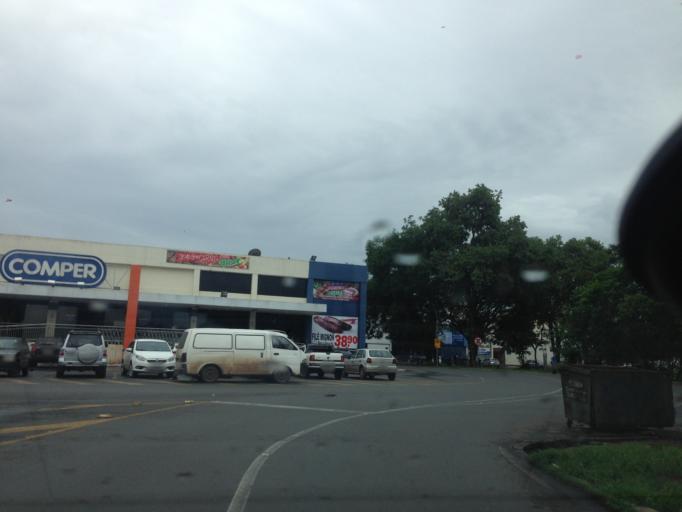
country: BR
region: Federal District
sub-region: Brasilia
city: Brasilia
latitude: -15.8111
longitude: -47.9021
